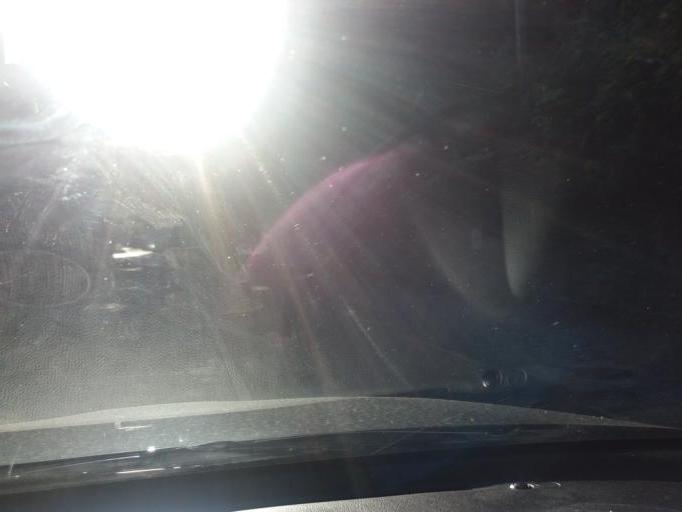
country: IE
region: Leinster
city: Lucan
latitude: 53.3688
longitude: -6.4333
